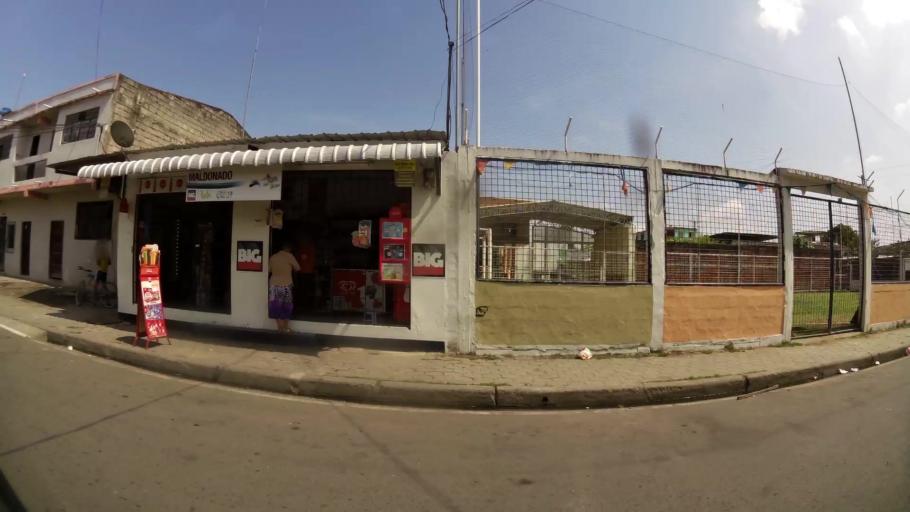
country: EC
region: Guayas
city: Eloy Alfaro
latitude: -2.1541
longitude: -79.8400
